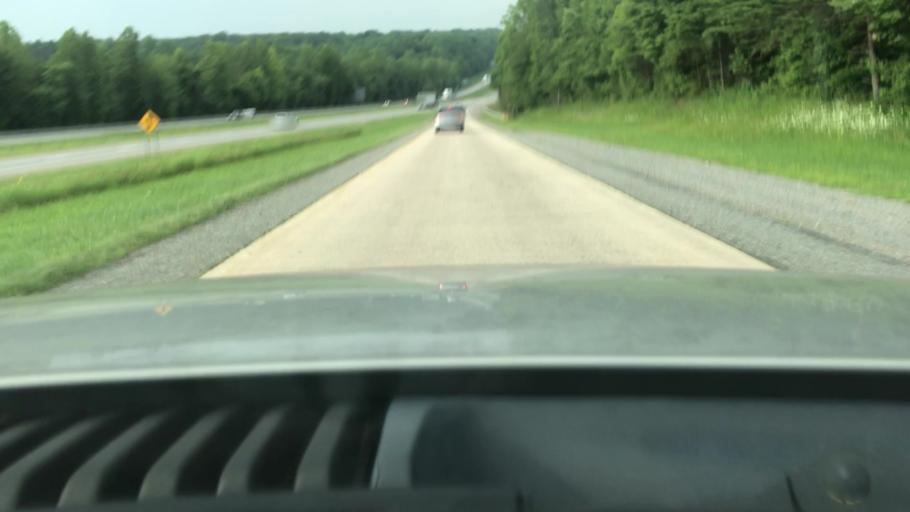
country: US
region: North Carolina
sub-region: Surry County
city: Elkin
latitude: 36.2830
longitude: -80.8195
